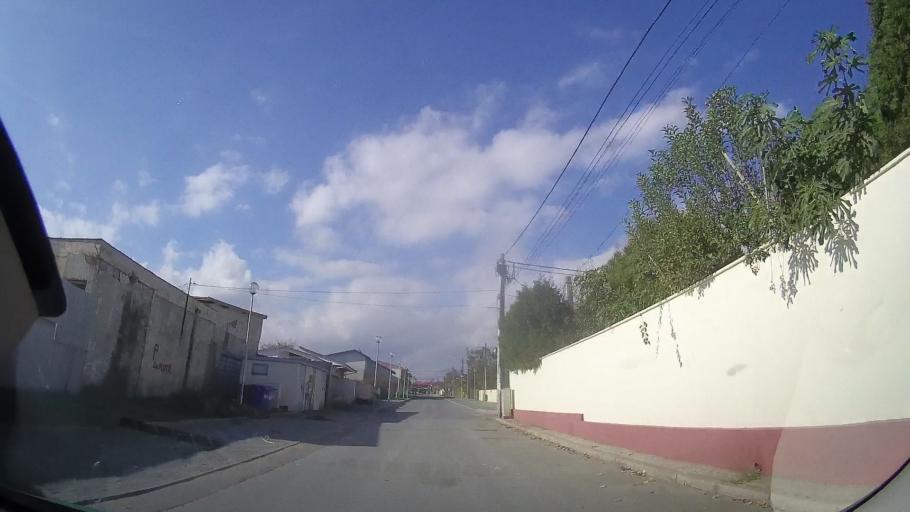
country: RO
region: Constanta
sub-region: Comuna Costinesti
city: Costinesti
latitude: 43.9527
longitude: 28.6384
